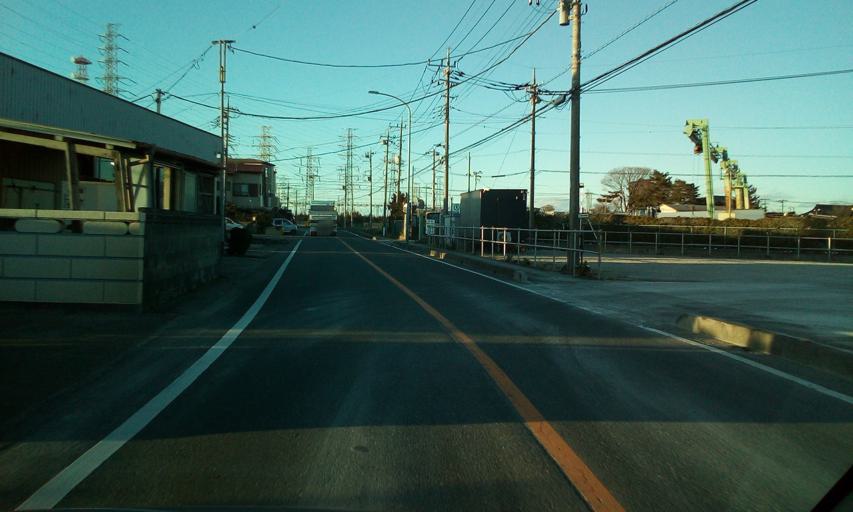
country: JP
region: Chiba
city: Nagareyama
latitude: 35.8660
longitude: 139.8733
